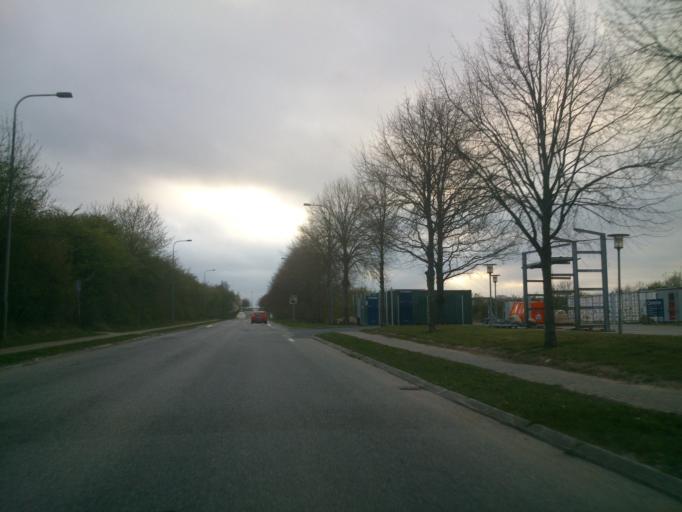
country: DK
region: South Denmark
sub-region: Fredericia Kommune
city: Fredericia
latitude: 55.5673
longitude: 9.7121
